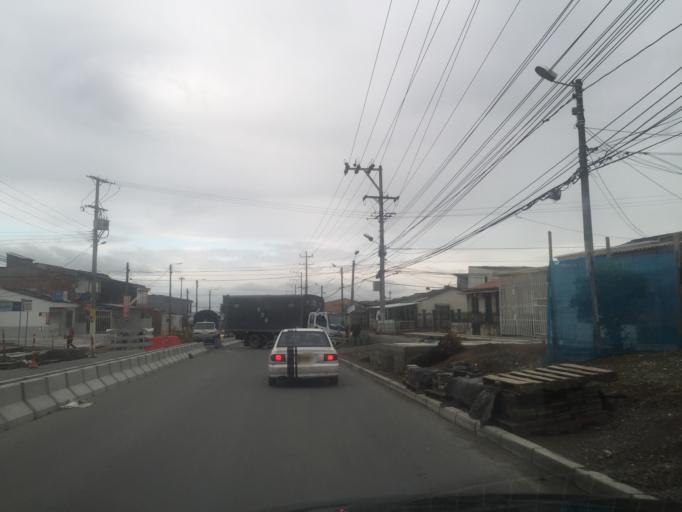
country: CO
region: Quindio
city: Armenia
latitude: 4.5197
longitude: -75.7070
